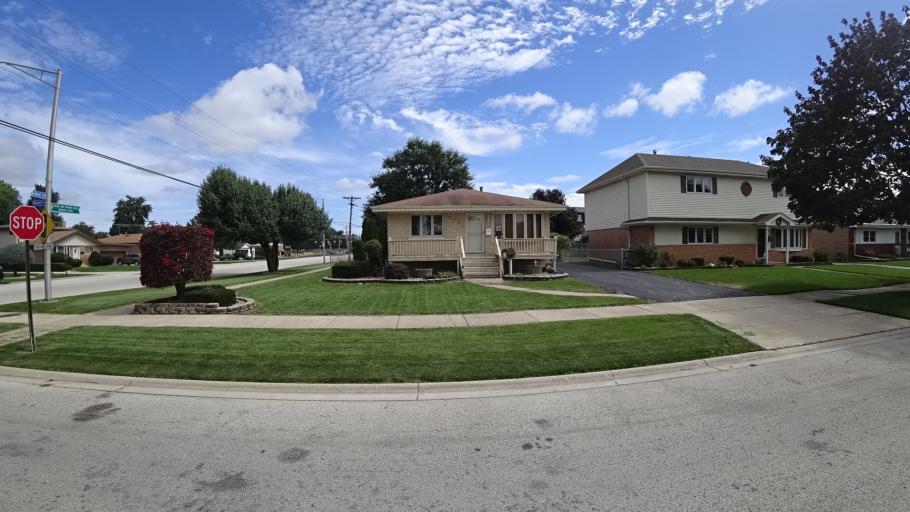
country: US
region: Illinois
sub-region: Cook County
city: Chicago Ridge
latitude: 41.7047
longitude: -87.7812
